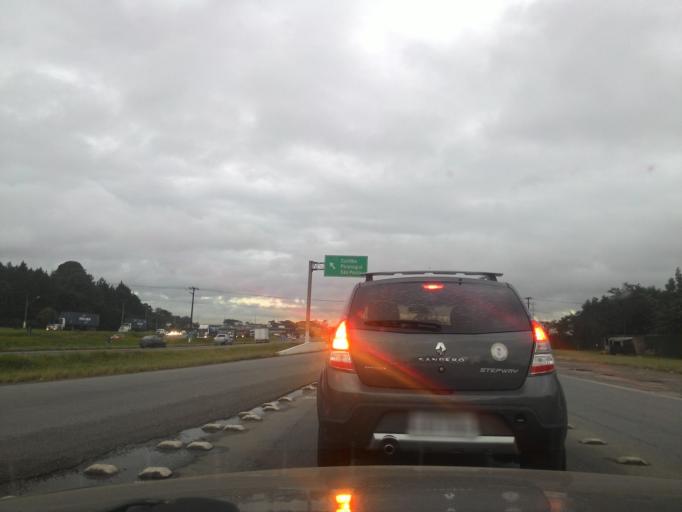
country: BR
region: Parana
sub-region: Sao Jose Dos Pinhais
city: Sao Jose dos Pinhais
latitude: -25.5426
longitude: -49.3094
